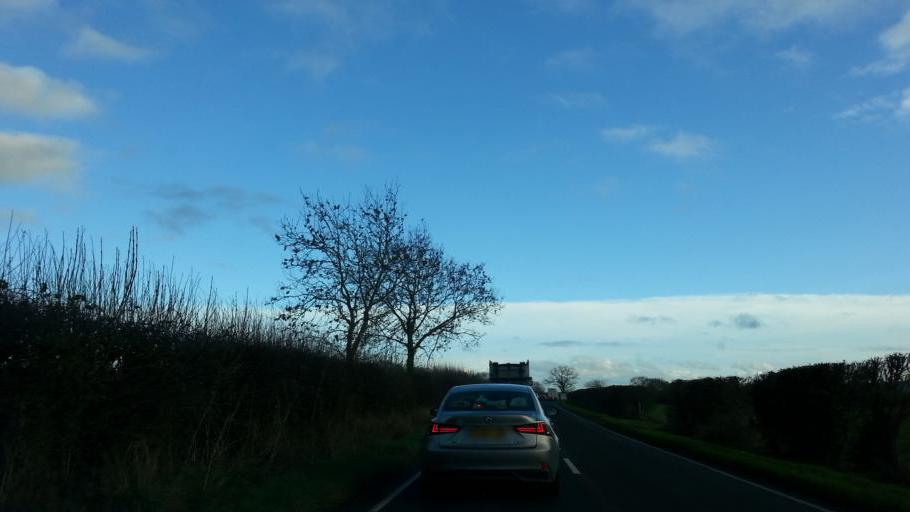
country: GB
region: England
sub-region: Oxfordshire
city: Shrivenham
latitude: 51.6149
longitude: -1.6221
